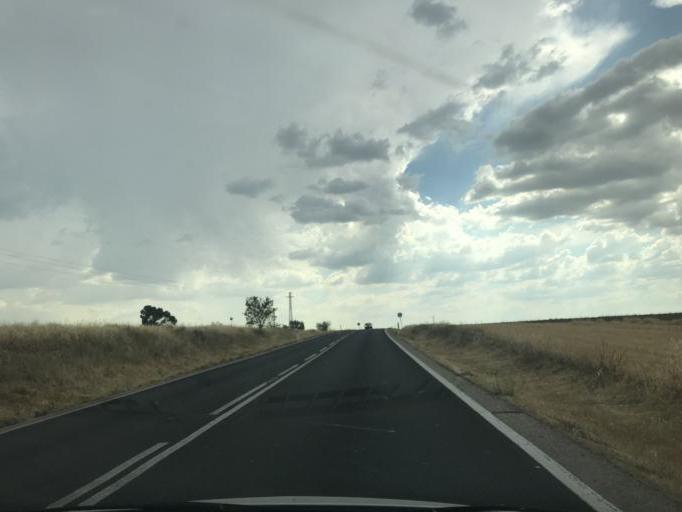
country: ES
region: Madrid
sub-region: Provincia de Madrid
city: Paracuellos de Jarama
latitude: 40.5141
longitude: -3.5075
